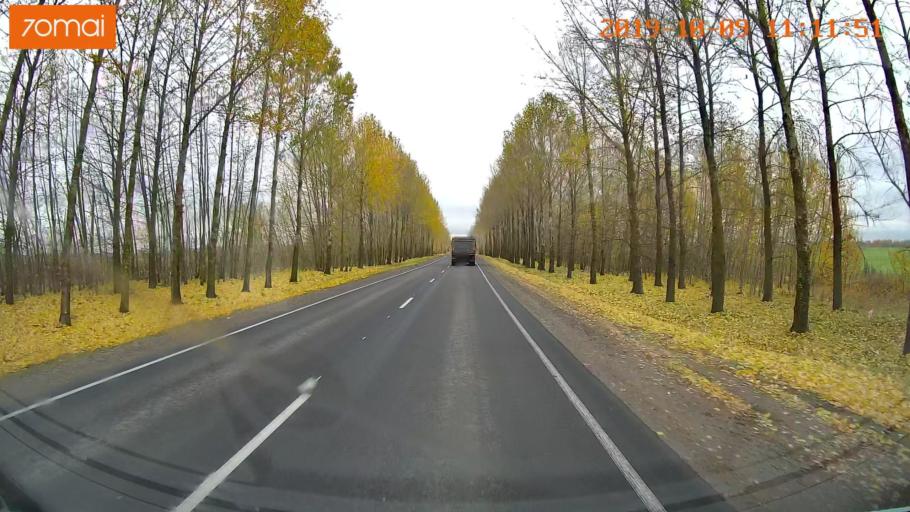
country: RU
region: Vologda
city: Vologda
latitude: 59.1721
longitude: 39.8244
